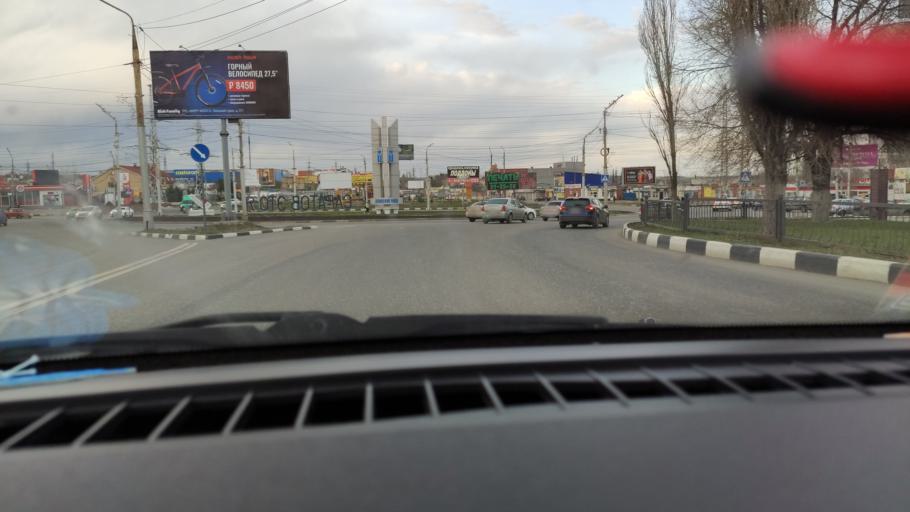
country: RU
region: Saratov
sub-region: Saratovskiy Rayon
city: Saratov
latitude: 51.6152
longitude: 45.9714
